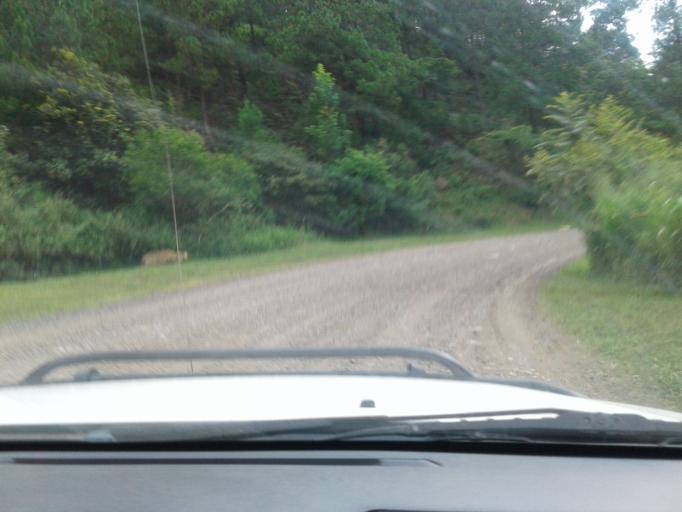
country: NI
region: Matagalpa
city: San Ramon
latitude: 12.9117
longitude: -85.7797
